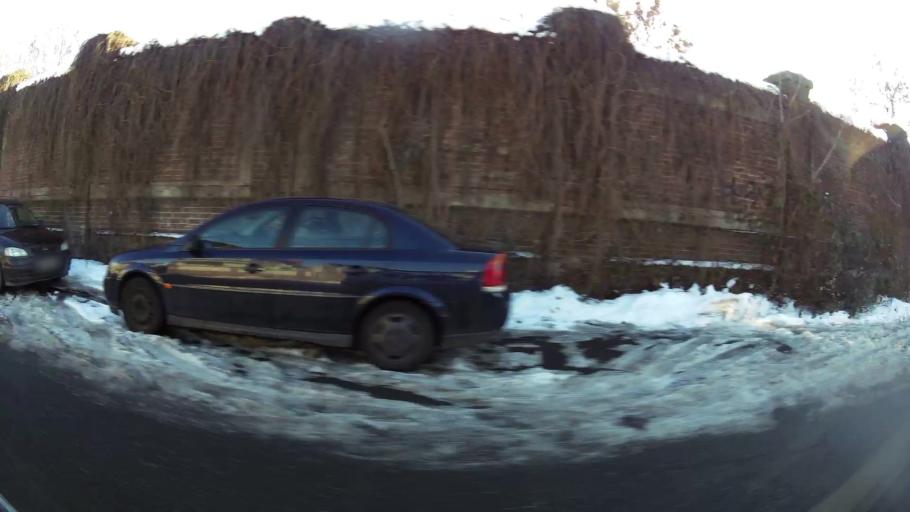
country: RO
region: Bucuresti
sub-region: Municipiul Bucuresti
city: Bucuresti
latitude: 44.4209
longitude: 26.0817
